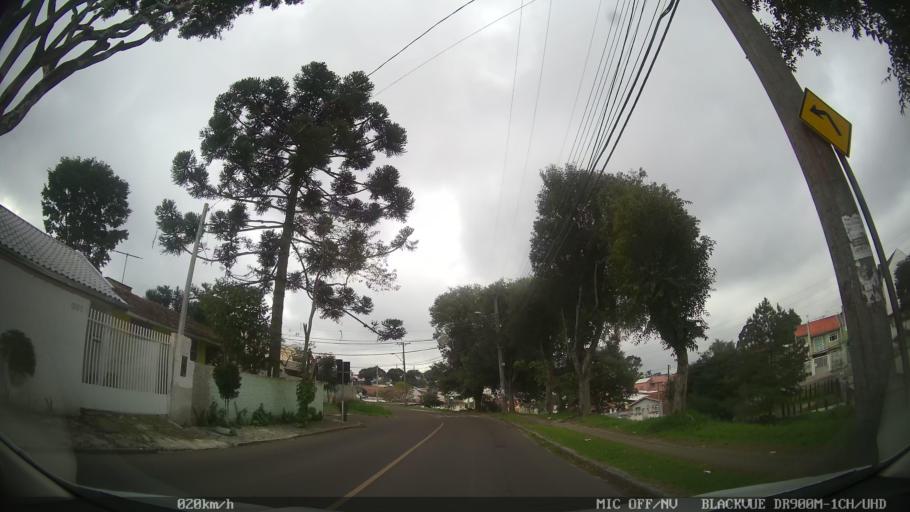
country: BR
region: Parana
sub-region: Curitiba
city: Curitiba
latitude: -25.3782
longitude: -49.2562
